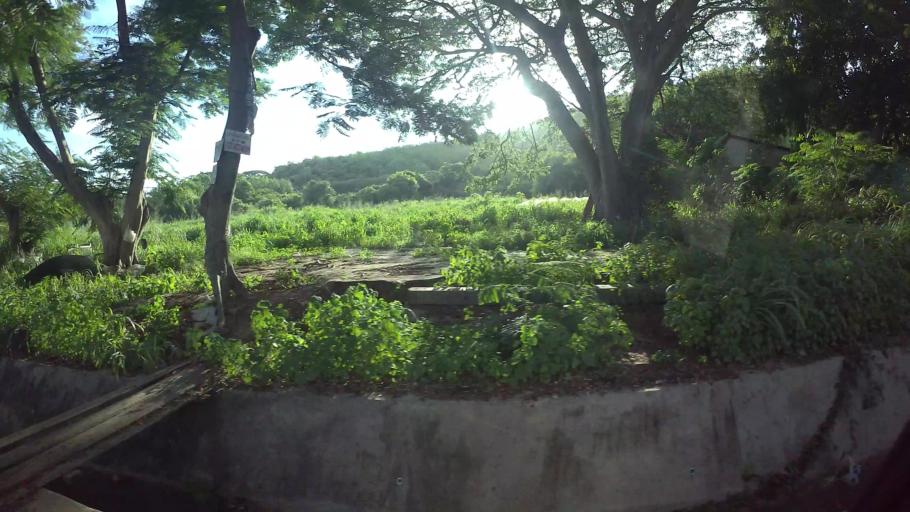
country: TH
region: Chon Buri
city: Sattahip
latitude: 12.6684
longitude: 100.9279
